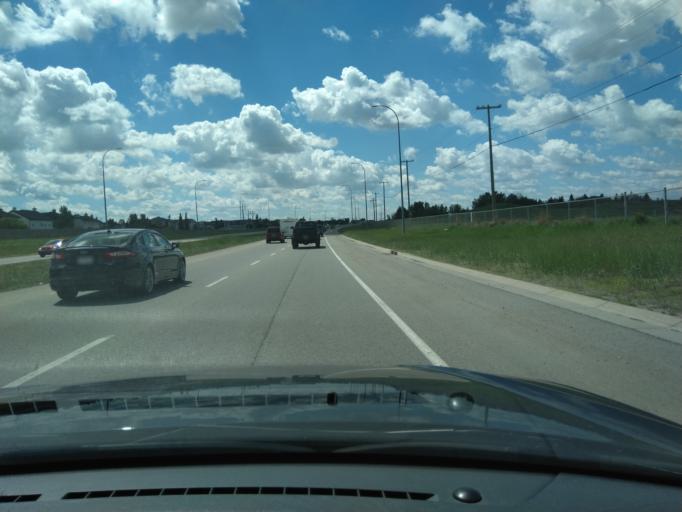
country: CA
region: Alberta
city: Calgary
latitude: 51.1204
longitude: -113.9702
